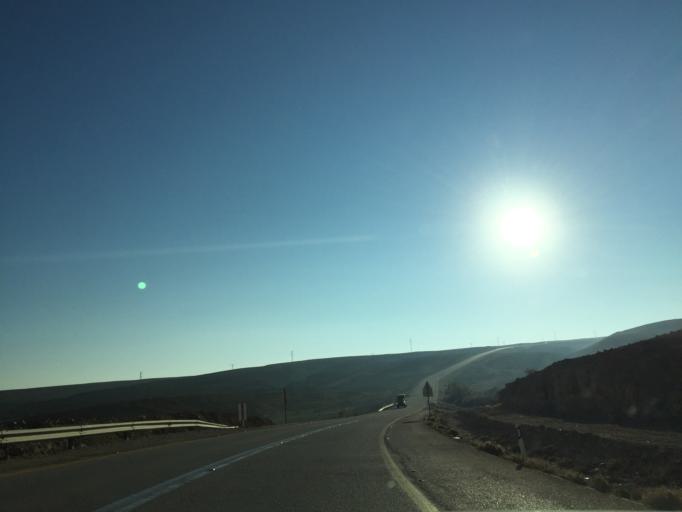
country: IL
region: Southern District
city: Mitzpe Ramon
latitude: 30.5289
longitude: 34.9282
